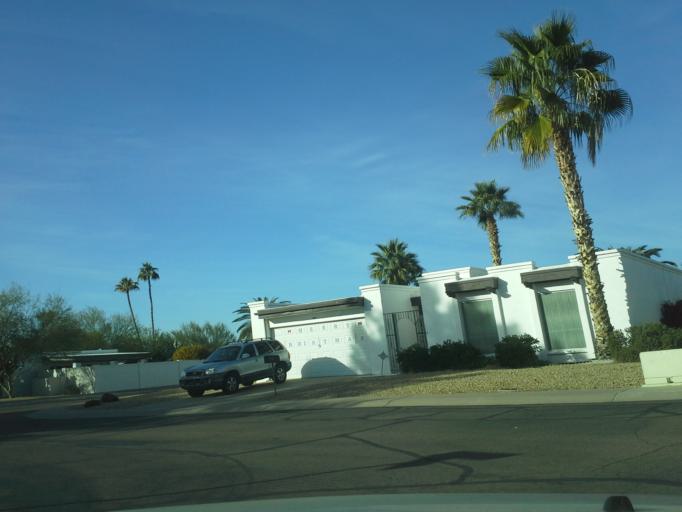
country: US
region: Arizona
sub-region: Maricopa County
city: Glendale
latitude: 33.6126
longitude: -112.0673
